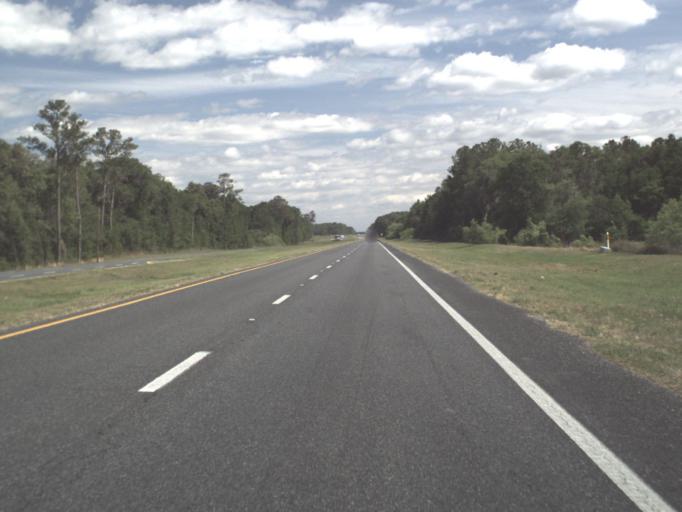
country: US
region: Florida
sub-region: Levy County
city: Williston
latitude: 29.3227
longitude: -82.3722
